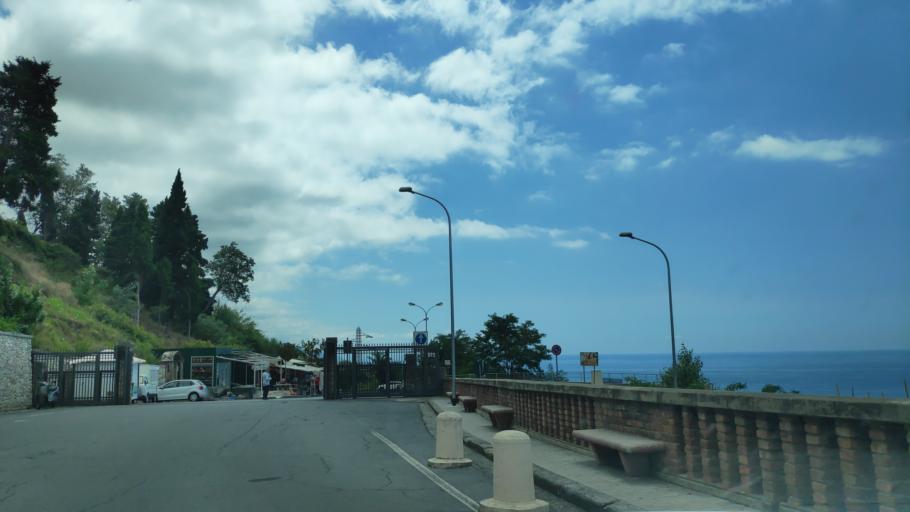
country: IT
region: Calabria
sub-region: Provincia di Cosenza
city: Paola
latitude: 39.3672
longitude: 16.0444
